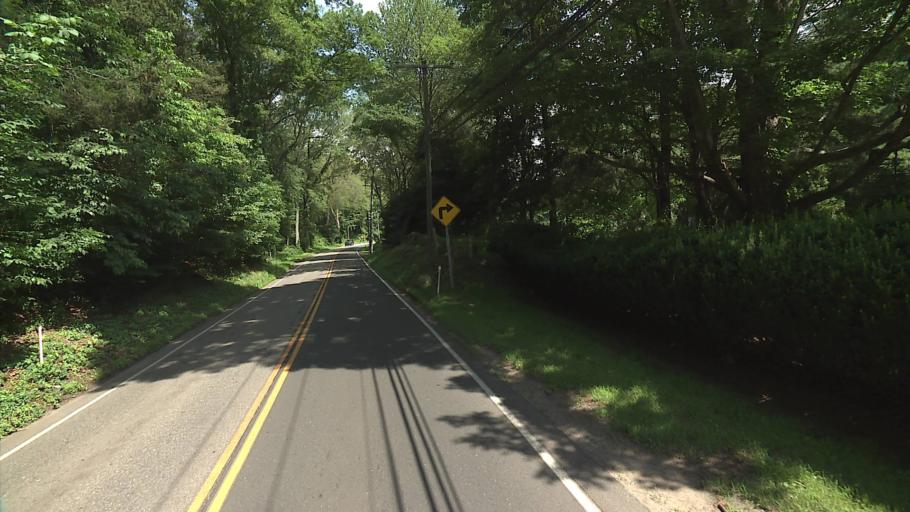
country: US
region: Connecticut
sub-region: Middlesex County
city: Essex Village
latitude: 41.3430
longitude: -72.4145
